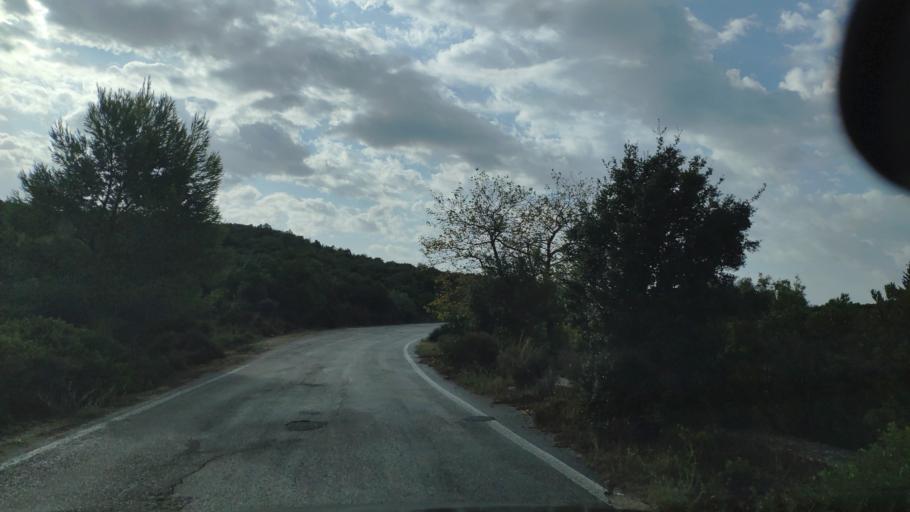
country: GR
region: West Greece
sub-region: Nomos Aitolias kai Akarnanias
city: Sardinia
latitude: 38.8809
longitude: 21.2469
